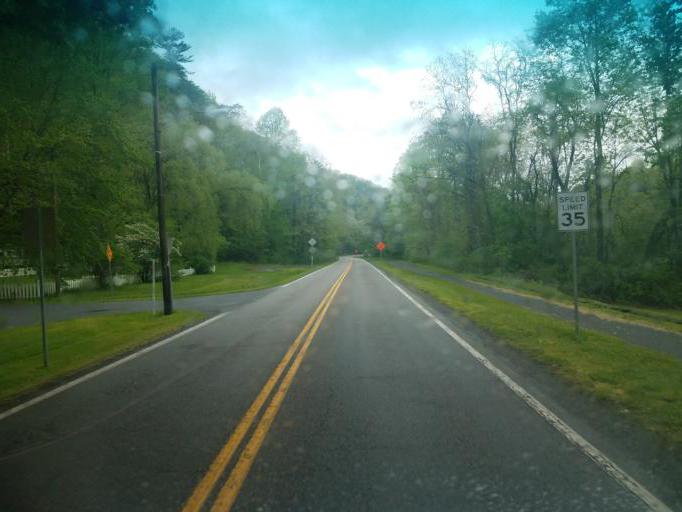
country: US
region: Virginia
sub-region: Washington County
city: Emory
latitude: 36.6302
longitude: -81.7817
